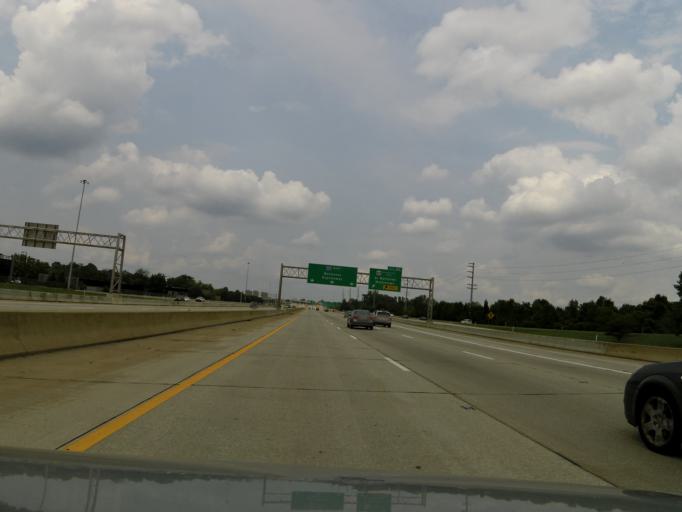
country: US
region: Kentucky
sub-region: Jefferson County
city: Saint Regis Park
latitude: 38.2397
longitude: -85.6226
